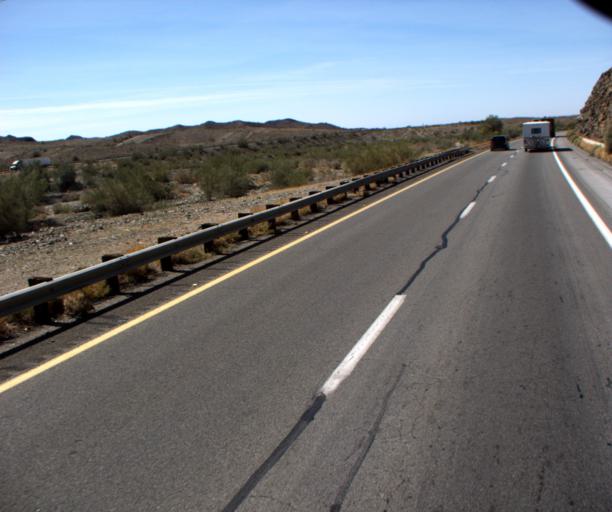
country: US
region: Arizona
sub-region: La Paz County
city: Ehrenberg
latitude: 33.6377
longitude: -114.3902
